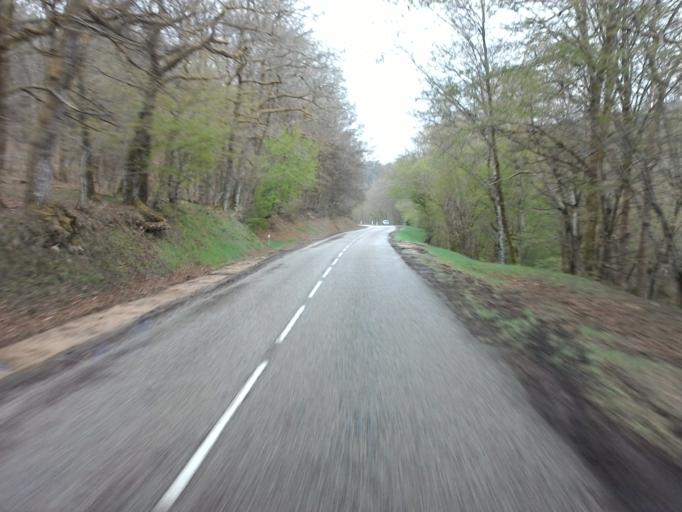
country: FR
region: Bourgogne
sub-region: Departement de la Cote-d'Or
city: Saulieu
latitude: 47.2460
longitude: 4.0529
